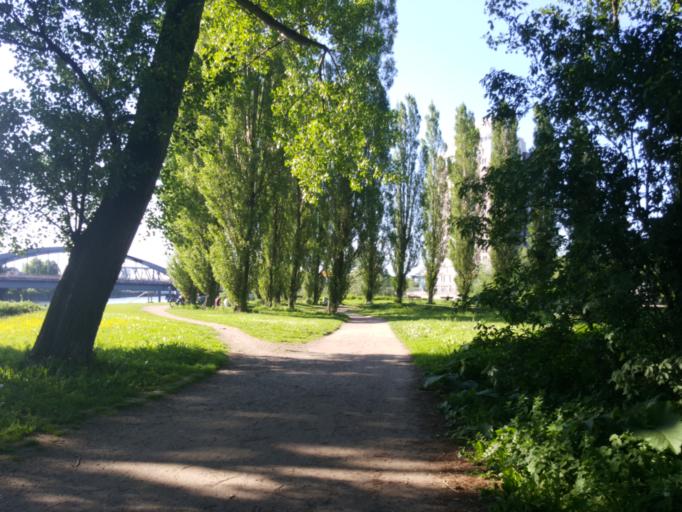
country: DE
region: Hamburg
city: Rothenburgsort
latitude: 53.5325
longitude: 10.0307
